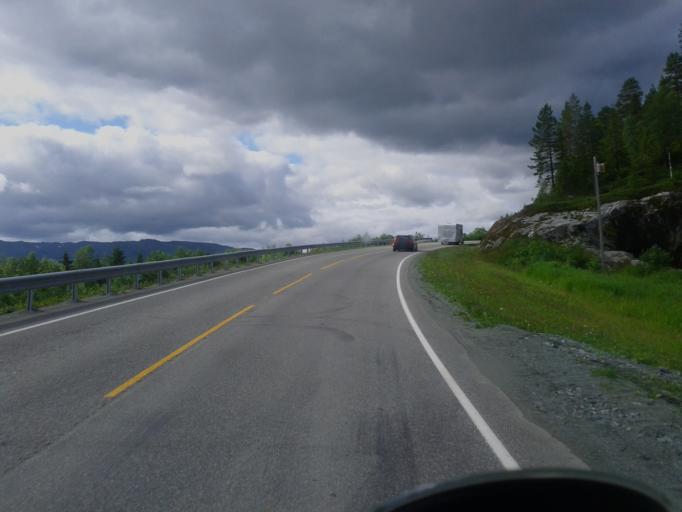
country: NO
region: Nord-Trondelag
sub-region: Grong
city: Grong
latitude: 64.5367
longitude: 12.4444
